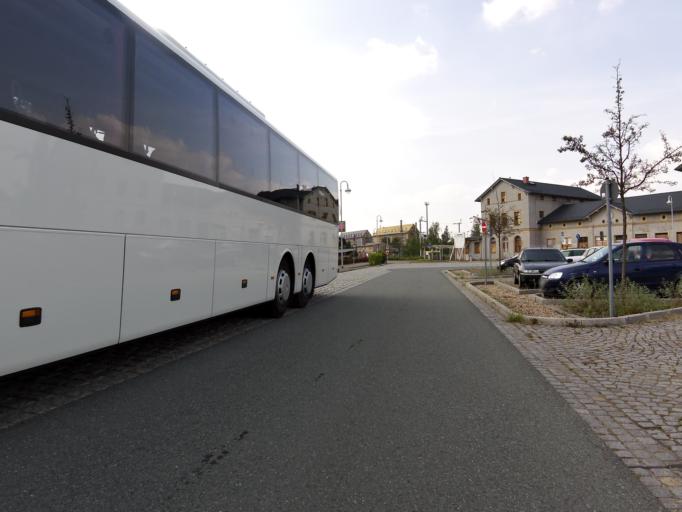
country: DE
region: Saxony
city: Oschatz
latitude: 51.3109
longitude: 13.1062
